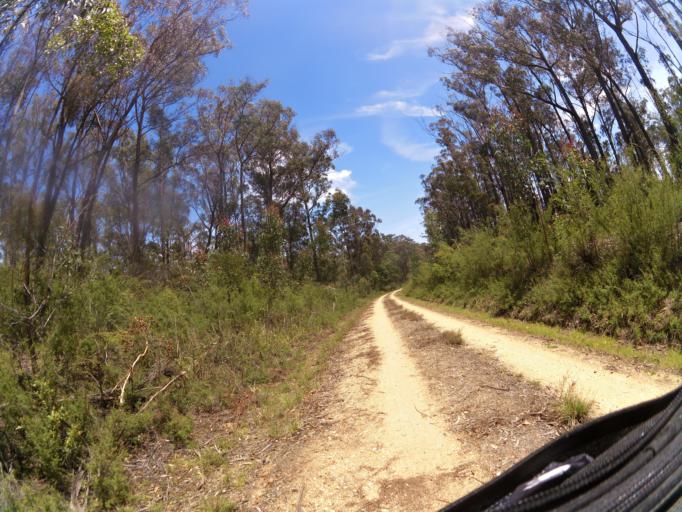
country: AU
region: Victoria
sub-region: East Gippsland
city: Lakes Entrance
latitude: -37.7589
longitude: 147.9552
